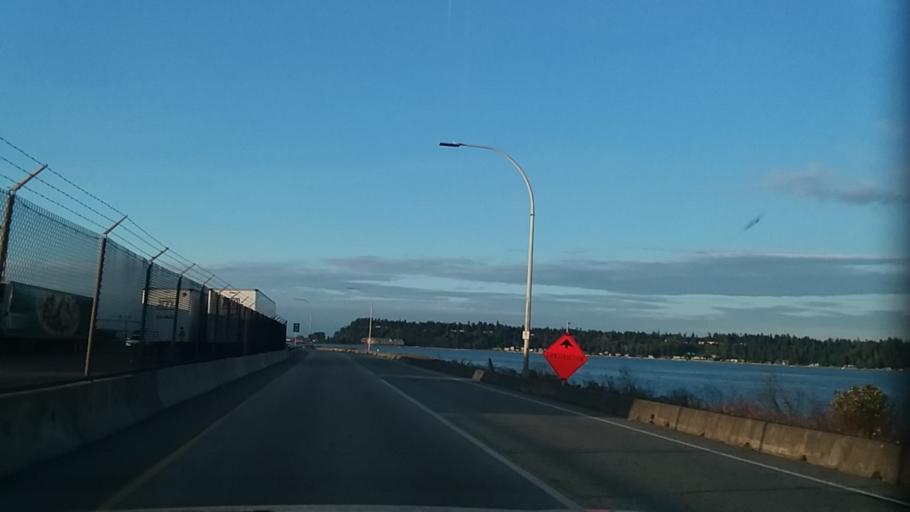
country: US
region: Washington
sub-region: Whatcom County
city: Point Roberts
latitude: 49.0088
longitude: -123.1251
